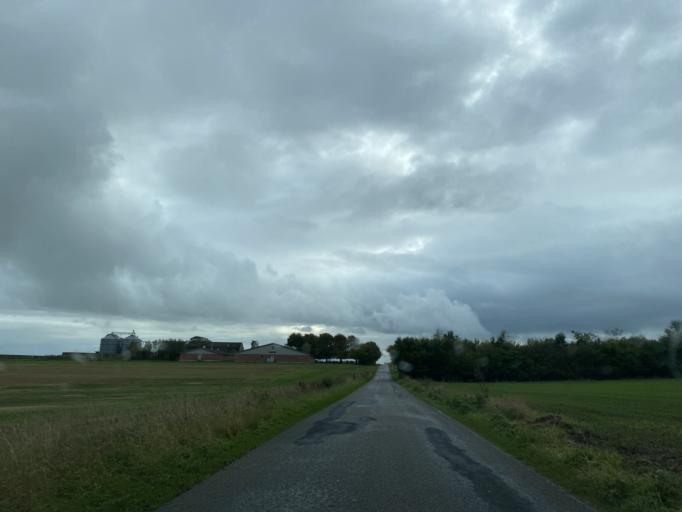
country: DK
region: Central Jutland
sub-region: Viborg Kommune
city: Bjerringbro
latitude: 56.3364
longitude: 9.7108
